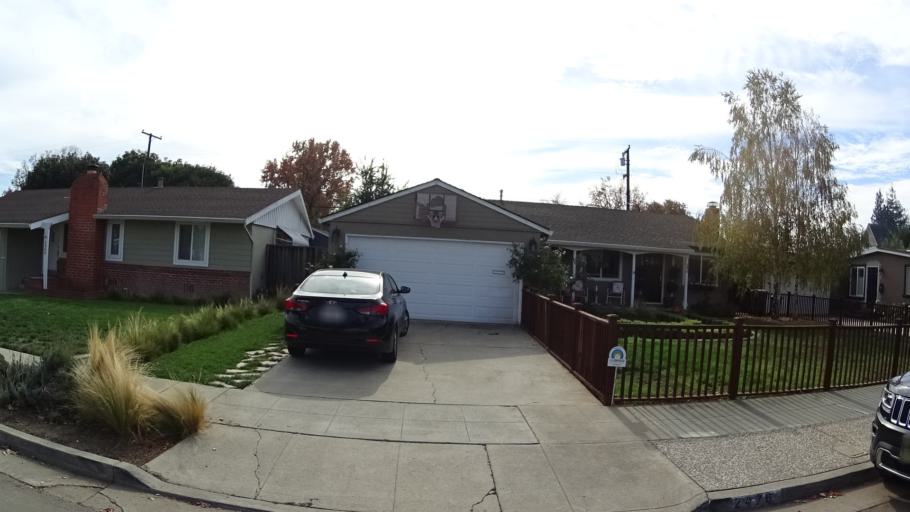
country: US
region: California
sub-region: Santa Clara County
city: Santa Clara
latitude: 37.3341
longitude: -121.9495
